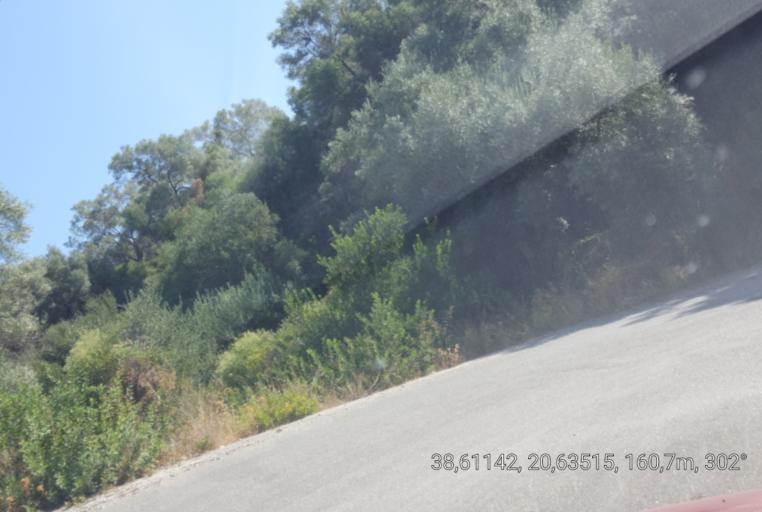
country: GR
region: Ionian Islands
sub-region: Lefkada
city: Nidri
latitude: 38.6114
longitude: 20.6353
